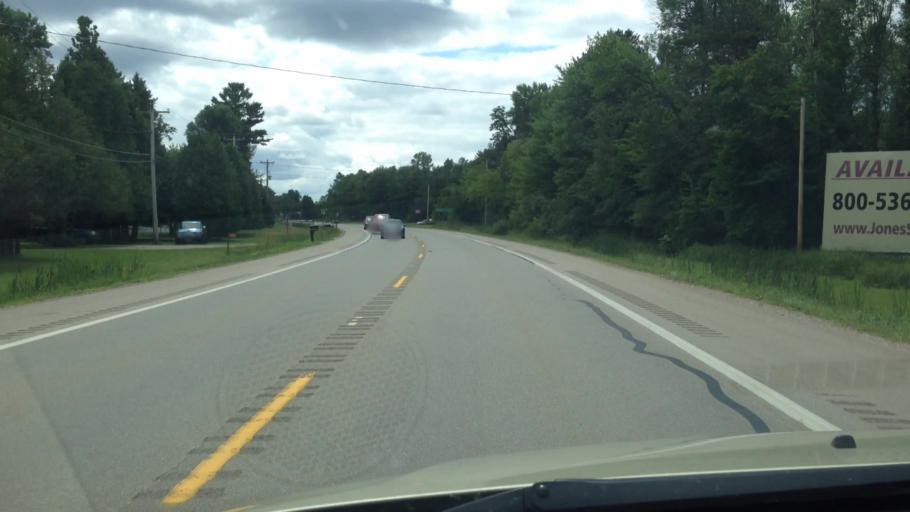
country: US
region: Michigan
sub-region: Menominee County
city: Menominee
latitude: 45.1802
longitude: -87.5684
